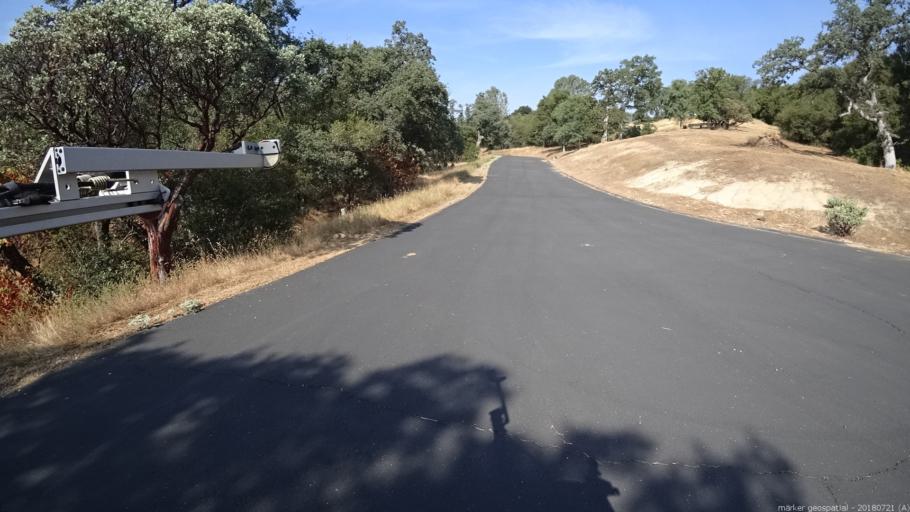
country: US
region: California
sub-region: Fresno County
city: Auberry
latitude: 37.2280
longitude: -119.5211
